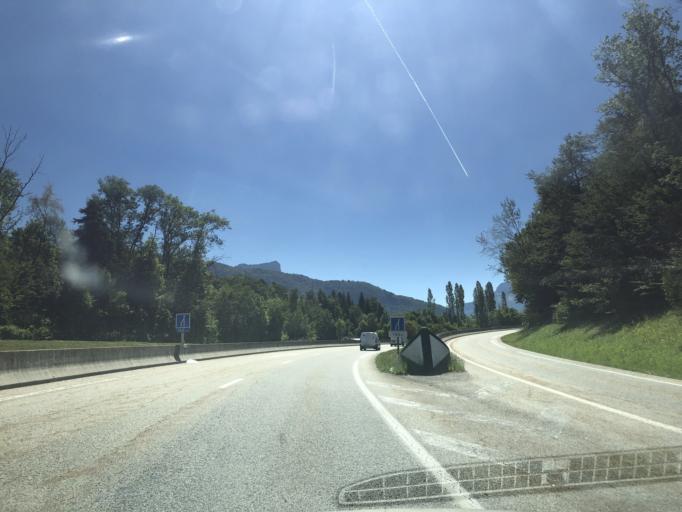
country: FR
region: Rhone-Alpes
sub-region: Departement de la Haute-Savoie
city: Villaz
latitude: 45.9355
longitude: 6.1695
